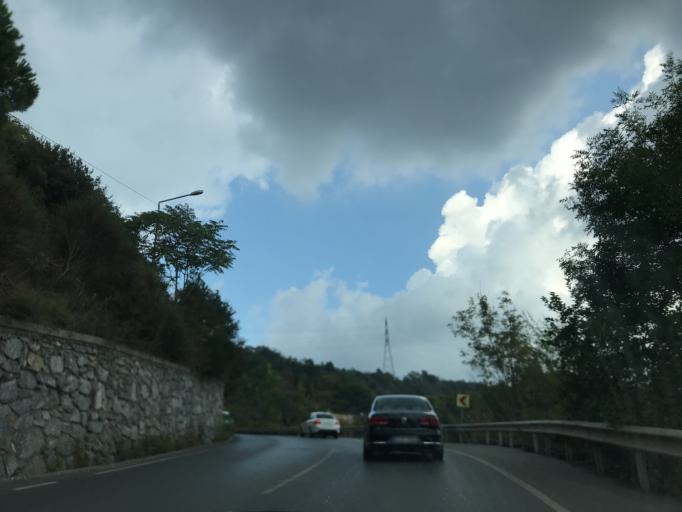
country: TR
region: Istanbul
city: Arikoey
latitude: 41.1819
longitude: 29.0453
